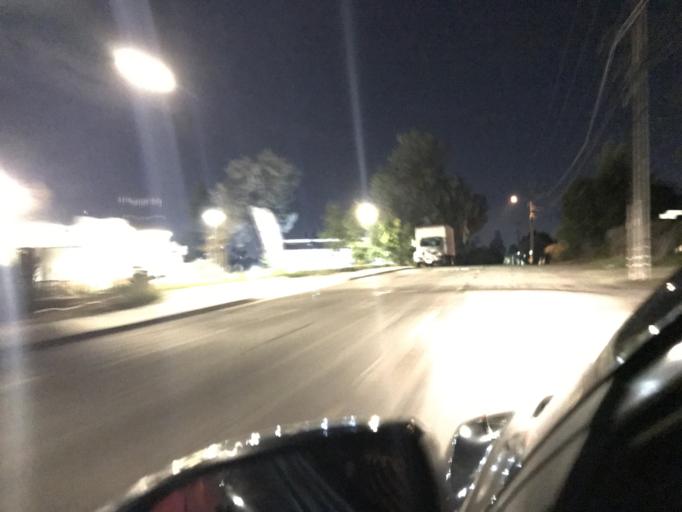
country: US
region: California
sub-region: San Diego County
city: La Mesa
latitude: 32.7816
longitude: -117.0346
